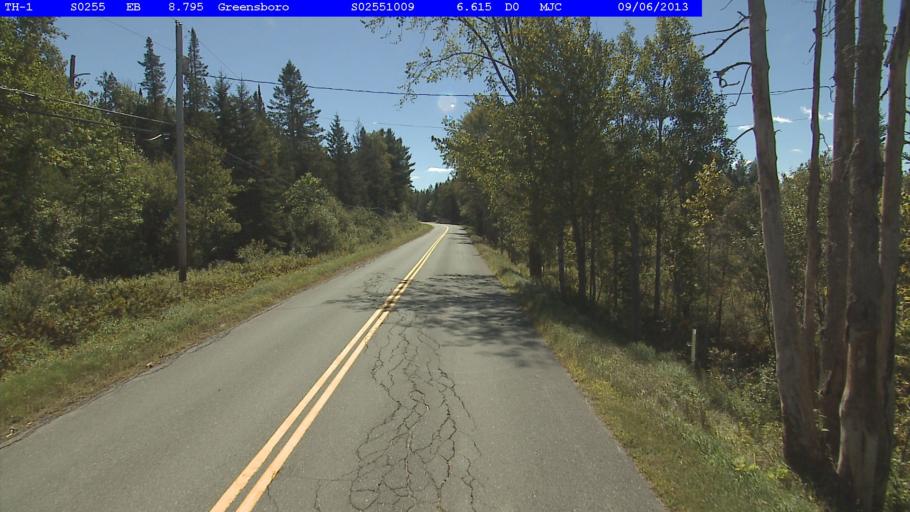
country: US
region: Vermont
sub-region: Caledonia County
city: Hardwick
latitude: 44.5590
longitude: -72.2775
